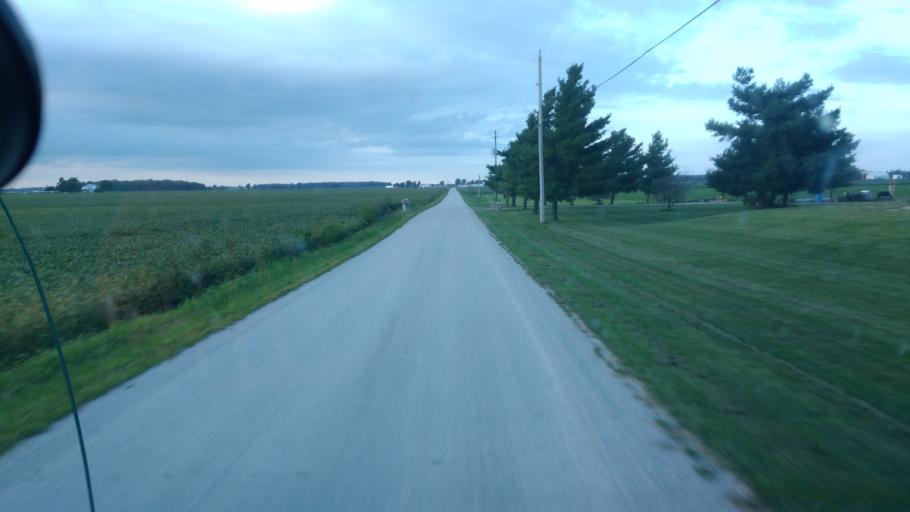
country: US
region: Ohio
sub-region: Hardin County
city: Kenton
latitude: 40.6662
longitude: -83.5146
